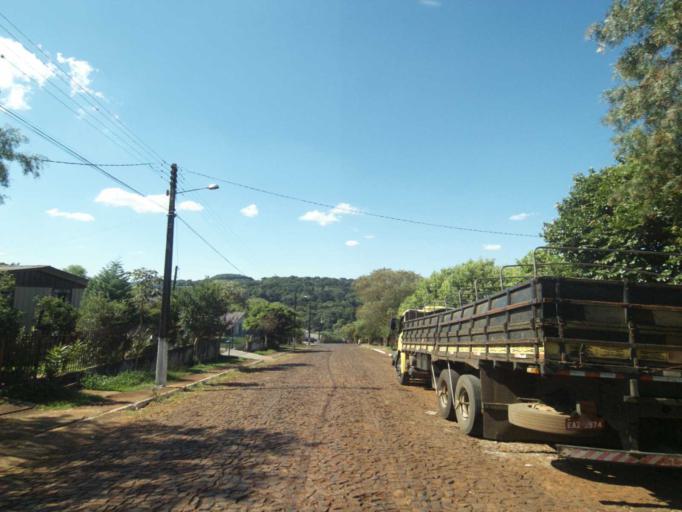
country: BR
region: Parana
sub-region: Laranjeiras Do Sul
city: Laranjeiras do Sul
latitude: -25.3816
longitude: -52.2058
